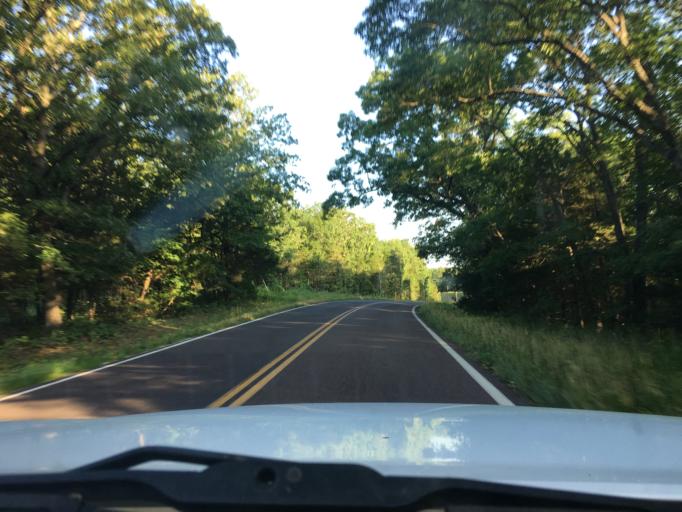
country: US
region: Missouri
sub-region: Gasconade County
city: Owensville
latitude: 38.4461
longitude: -91.6304
